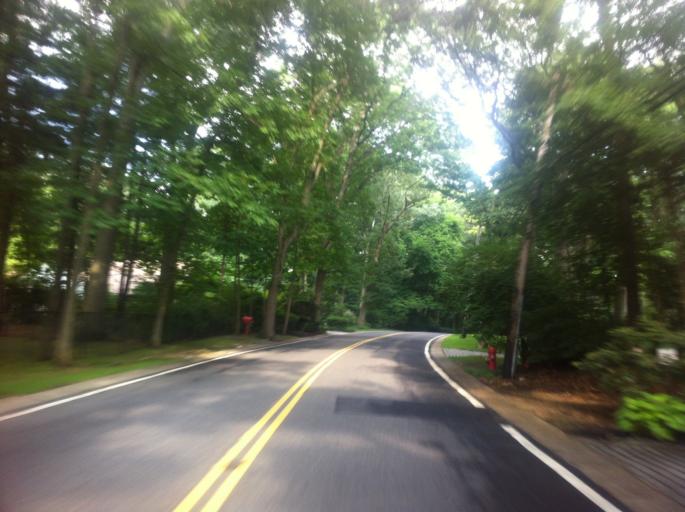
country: US
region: New York
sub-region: Nassau County
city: Old Brookville
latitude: 40.8522
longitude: -73.6068
